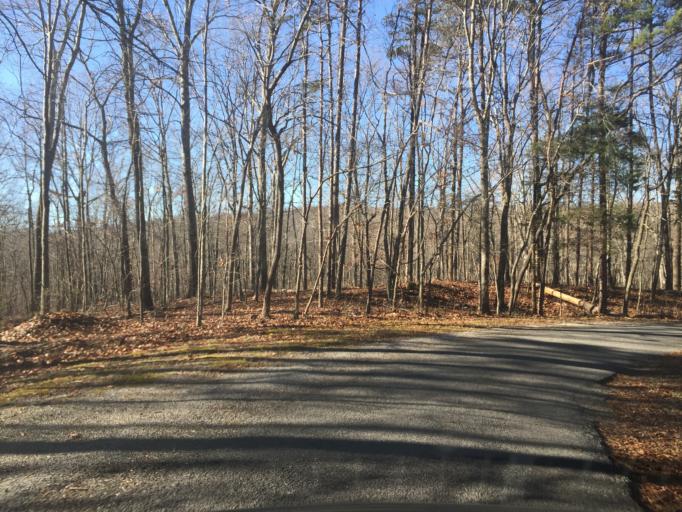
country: US
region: Tennessee
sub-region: Hamilton County
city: Harrison
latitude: 35.0978
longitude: -85.1141
